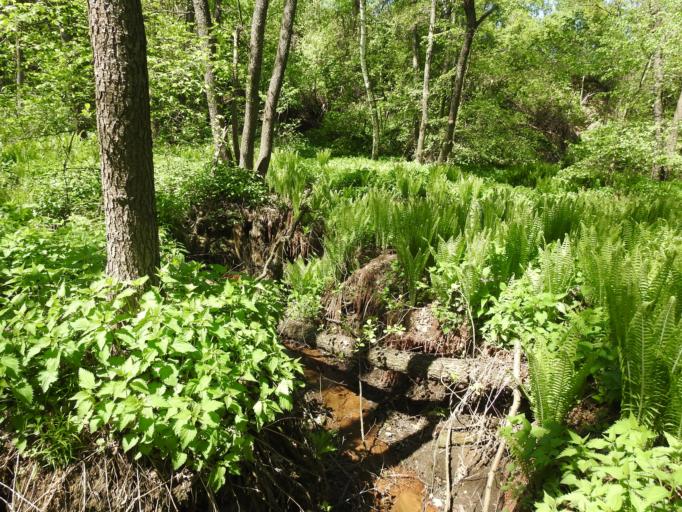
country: RU
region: Saratov
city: Krasnyy Oktyabr'
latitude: 51.5920
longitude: 45.7230
